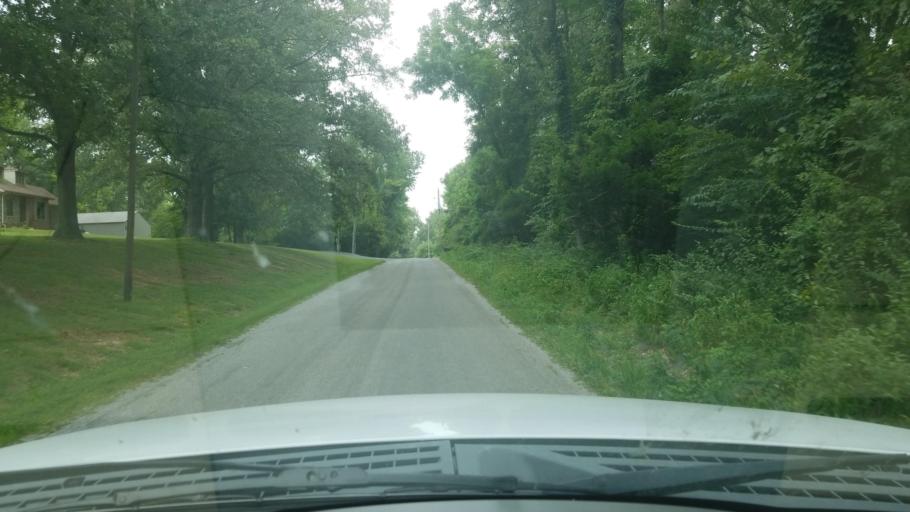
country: US
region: Illinois
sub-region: Saline County
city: Eldorado
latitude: 37.8256
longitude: -88.4477
